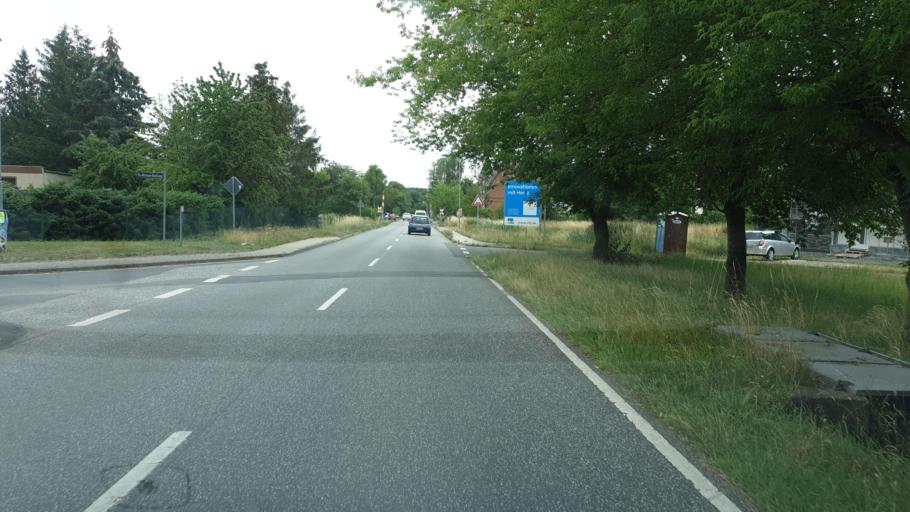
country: DE
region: Saxony-Anhalt
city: Querfurt
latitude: 51.3850
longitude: 11.5937
